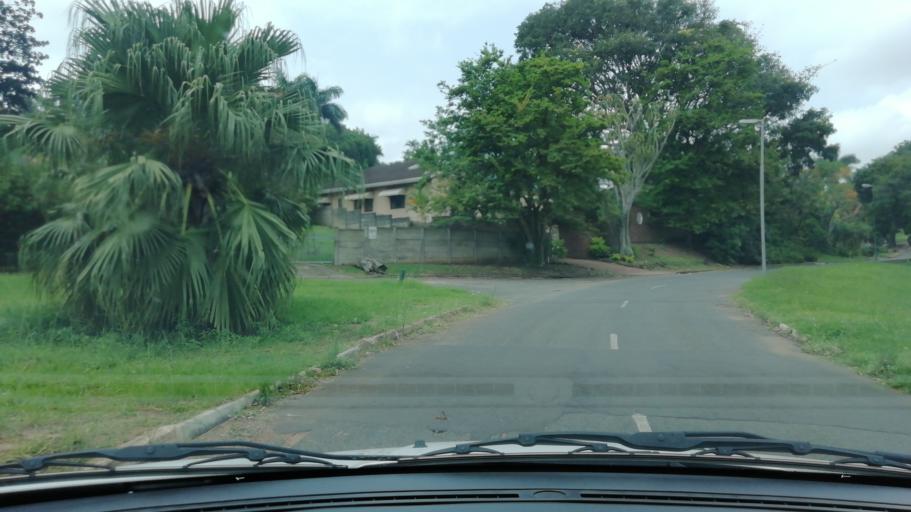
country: ZA
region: KwaZulu-Natal
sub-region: uThungulu District Municipality
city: Empangeni
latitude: -28.7538
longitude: 31.8900
